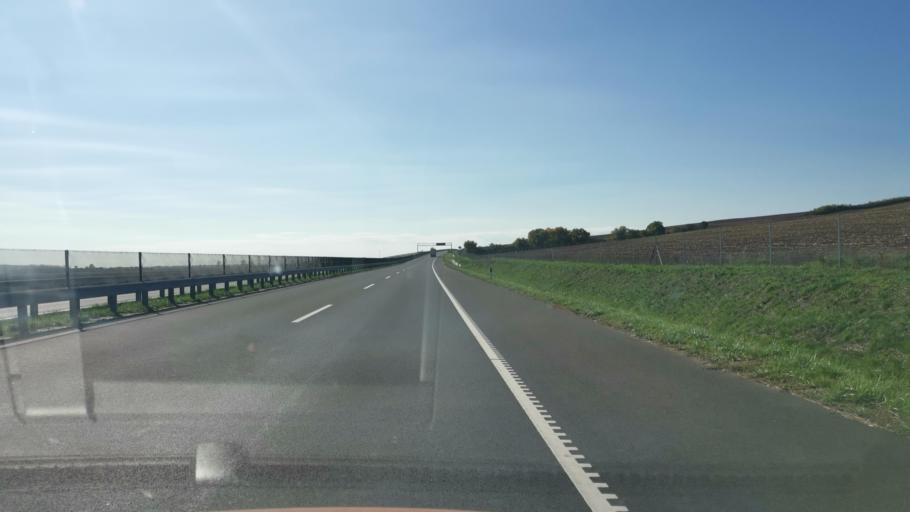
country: HU
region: Borsod-Abauj-Zemplen
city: Halmaj
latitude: 48.2701
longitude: 20.9984
